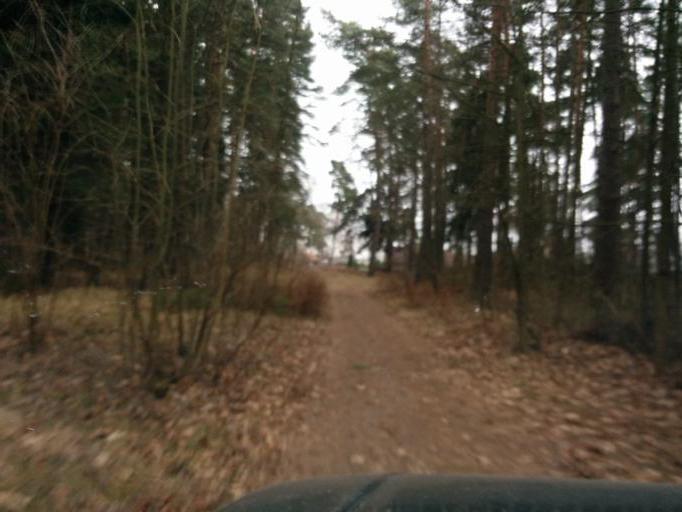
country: LV
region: Babite
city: Pinki
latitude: 56.9864
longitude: 23.8882
